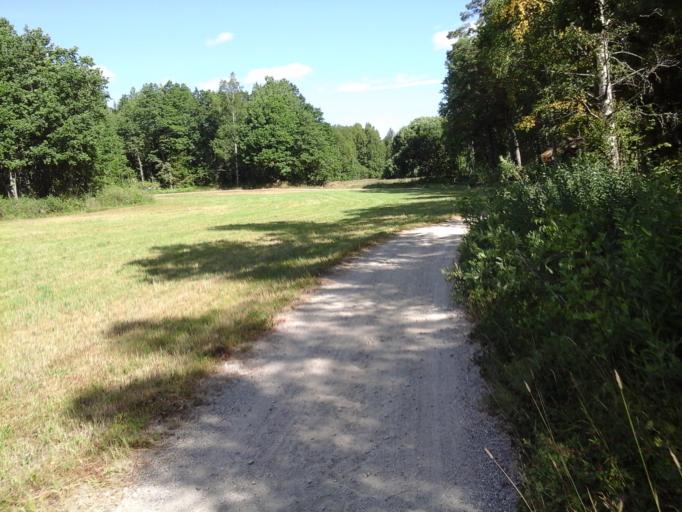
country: SE
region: Soedermanland
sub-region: Eskilstuna Kommun
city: Arla
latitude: 59.2471
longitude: 16.7685
